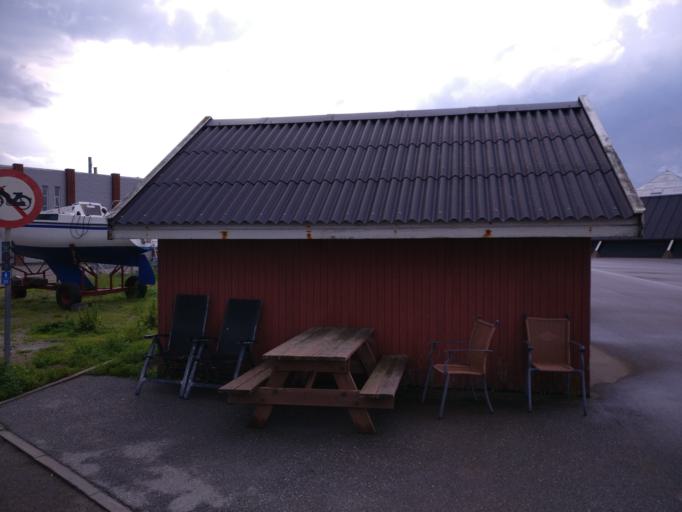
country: DK
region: North Denmark
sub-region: Frederikshavn Kommune
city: Saeby
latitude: 57.3318
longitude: 10.5341
